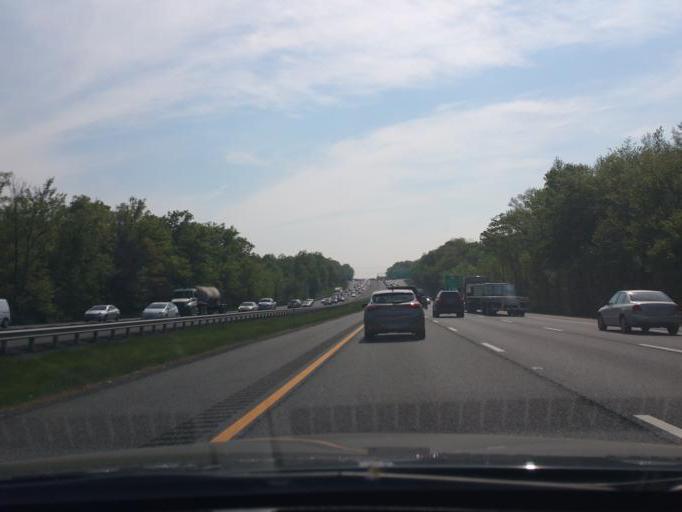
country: US
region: Maryland
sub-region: Harford County
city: Edgewood
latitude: 39.4625
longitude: -76.2968
